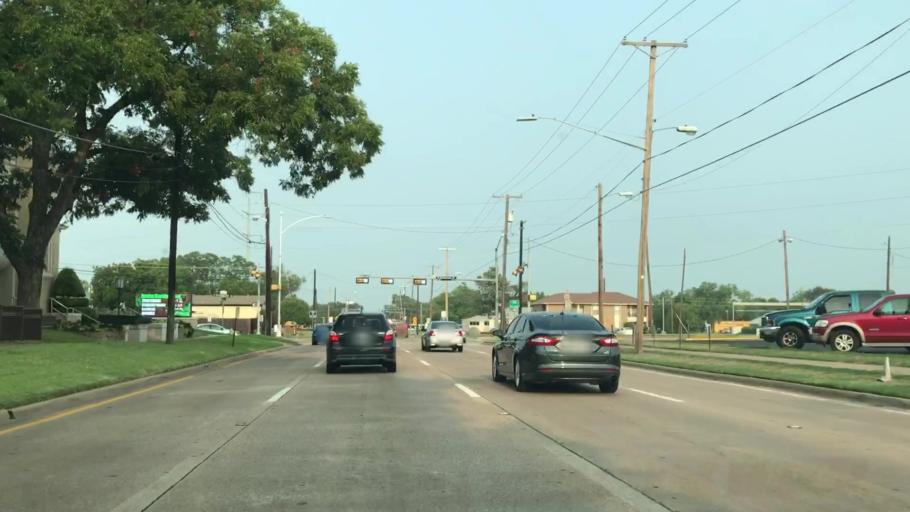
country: US
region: Texas
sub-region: Dallas County
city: Garland
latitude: 32.9090
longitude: -96.6411
